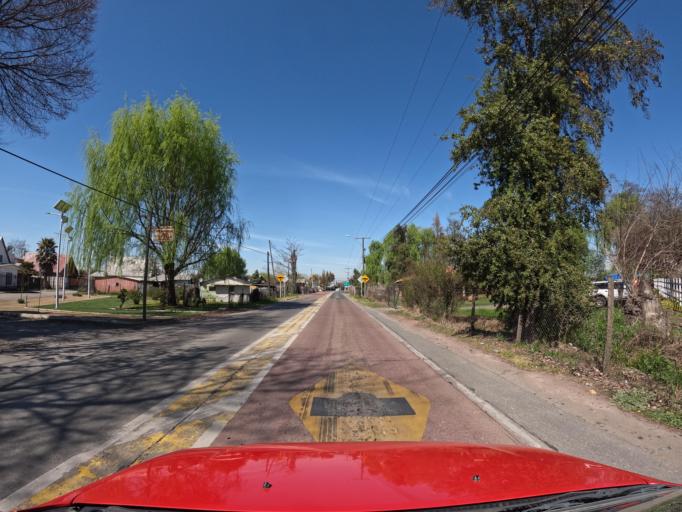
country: CL
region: Maule
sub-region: Provincia de Curico
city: Curico
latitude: -35.0126
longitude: -71.3128
